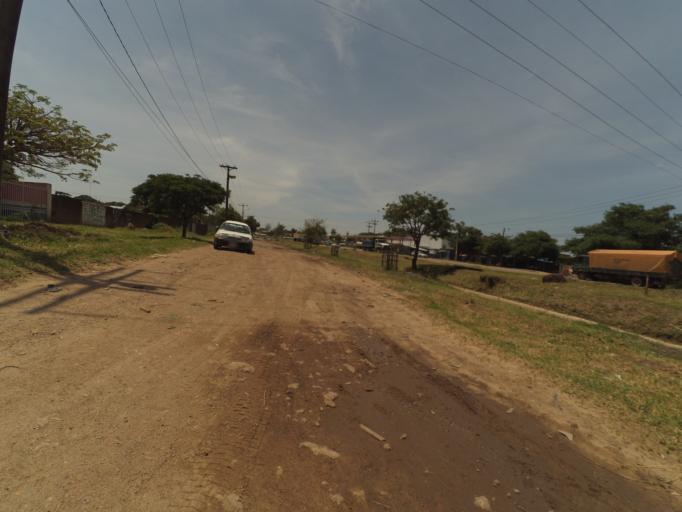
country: BO
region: Santa Cruz
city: Santa Cruz de la Sierra
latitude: -17.8366
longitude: -63.2385
